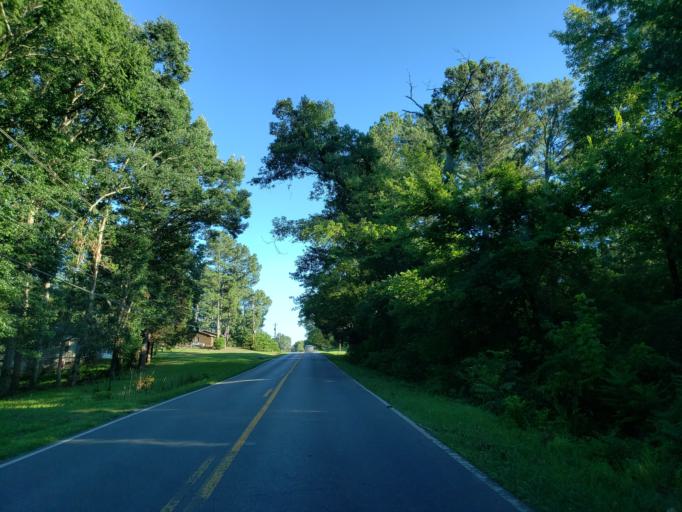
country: US
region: Georgia
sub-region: Polk County
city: Aragon
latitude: 34.0336
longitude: -85.0712
